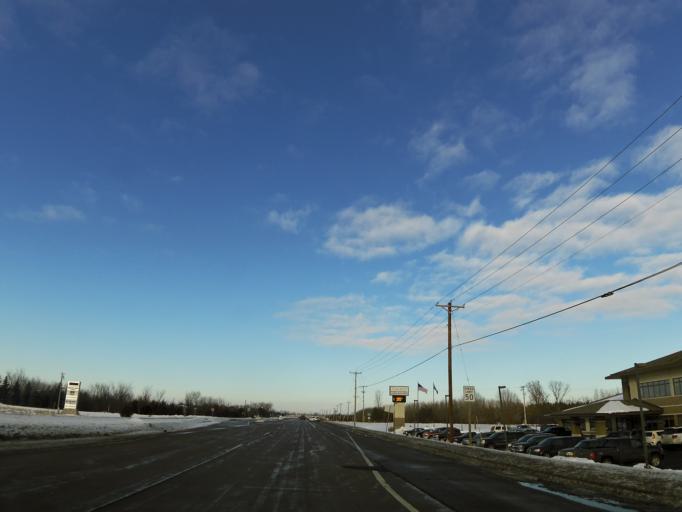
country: US
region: Wisconsin
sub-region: Saint Croix County
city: Hudson
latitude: 44.9693
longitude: -92.6798
